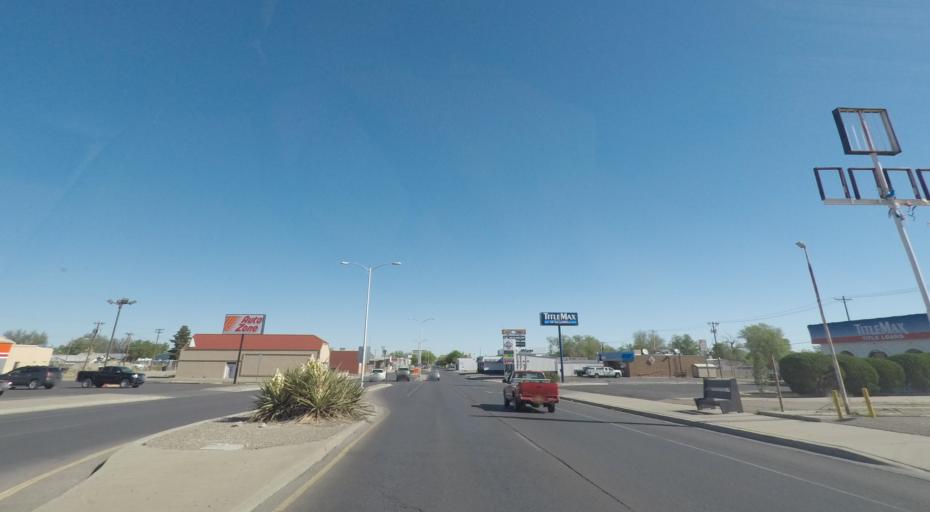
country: US
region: New Mexico
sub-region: Chaves County
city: Roswell
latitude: 33.3861
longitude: -104.5227
